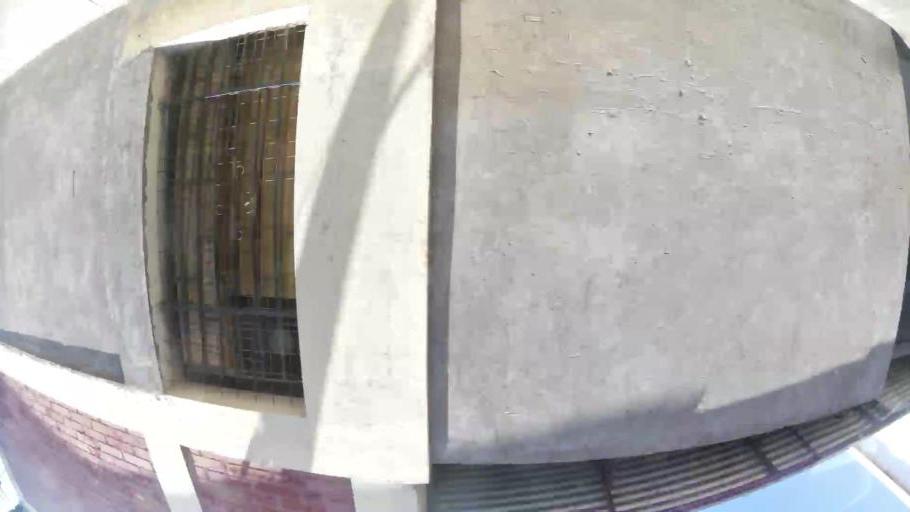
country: CL
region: Santiago Metropolitan
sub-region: Provincia de Maipo
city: San Bernardo
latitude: -33.5879
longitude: -70.6750
